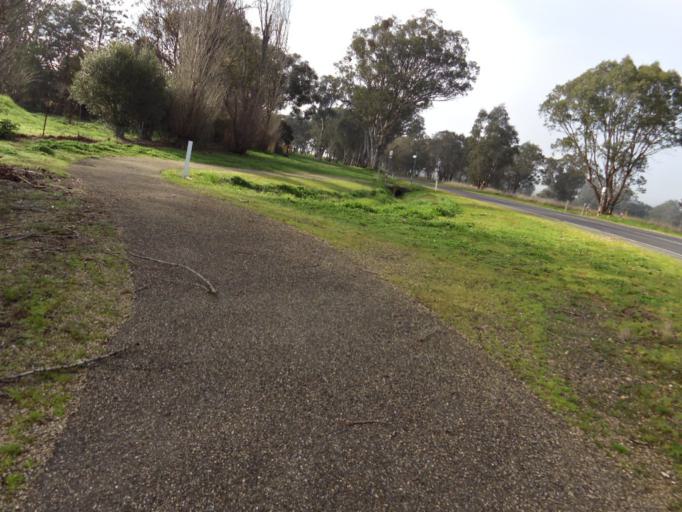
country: AU
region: Victoria
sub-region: Wangaratta
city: Wangaratta
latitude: -36.4532
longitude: 146.5542
